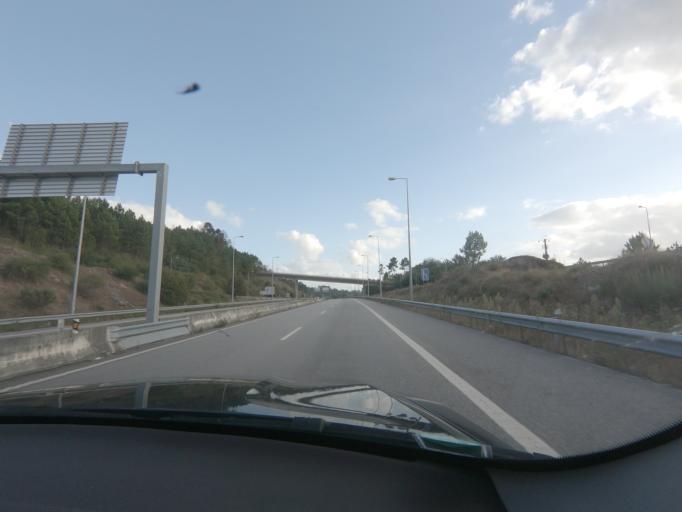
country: PT
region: Viseu
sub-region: Viseu
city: Viseu
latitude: 40.6242
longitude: -7.9622
